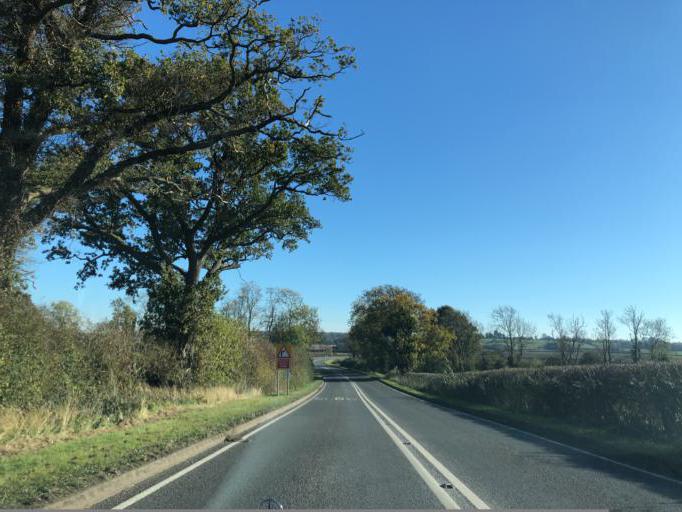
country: GB
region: England
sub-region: Warwickshire
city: Harbury
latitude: 52.2653
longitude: -1.4657
